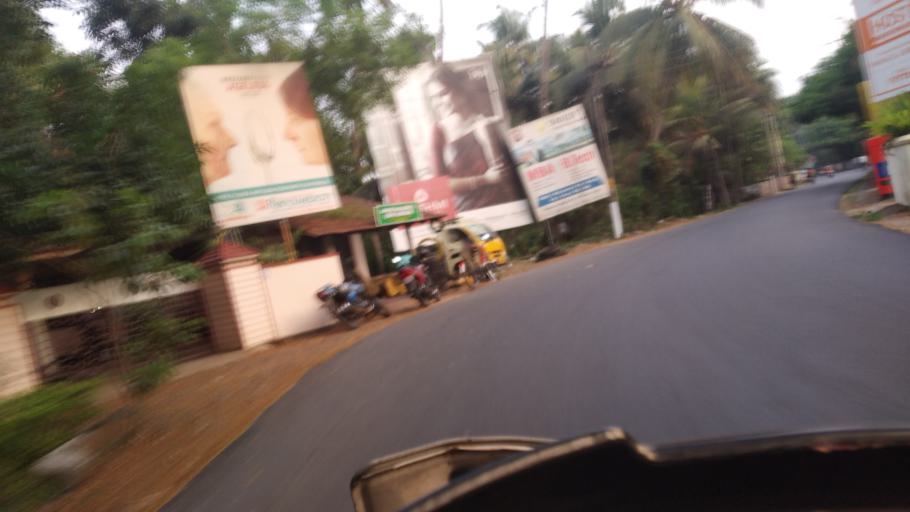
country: IN
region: Kerala
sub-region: Thrissur District
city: Kodungallur
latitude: 10.1846
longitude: 76.2045
